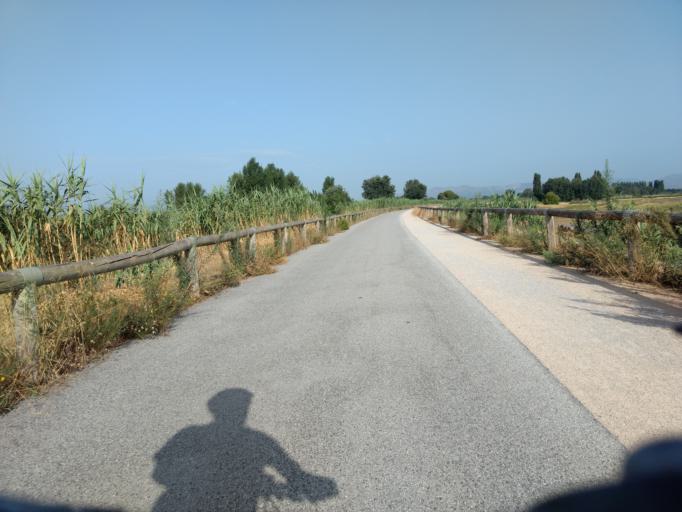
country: FR
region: Languedoc-Roussillon
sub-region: Departement des Pyrenees-Orientales
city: Claira
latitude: 42.7538
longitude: 2.9431
